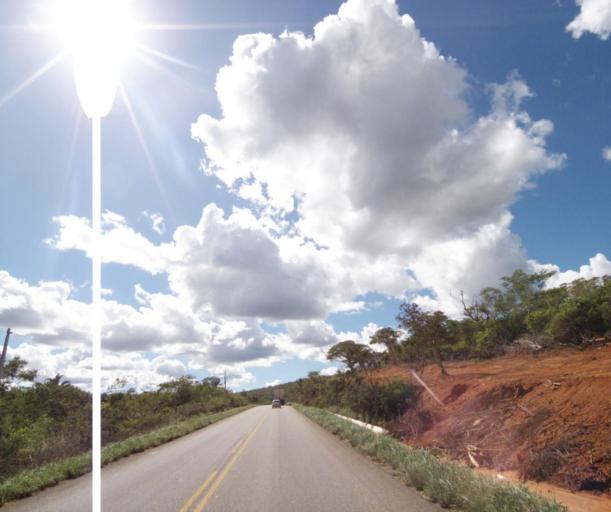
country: BR
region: Bahia
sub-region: Caetite
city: Caetite
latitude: -14.1448
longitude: -42.3653
